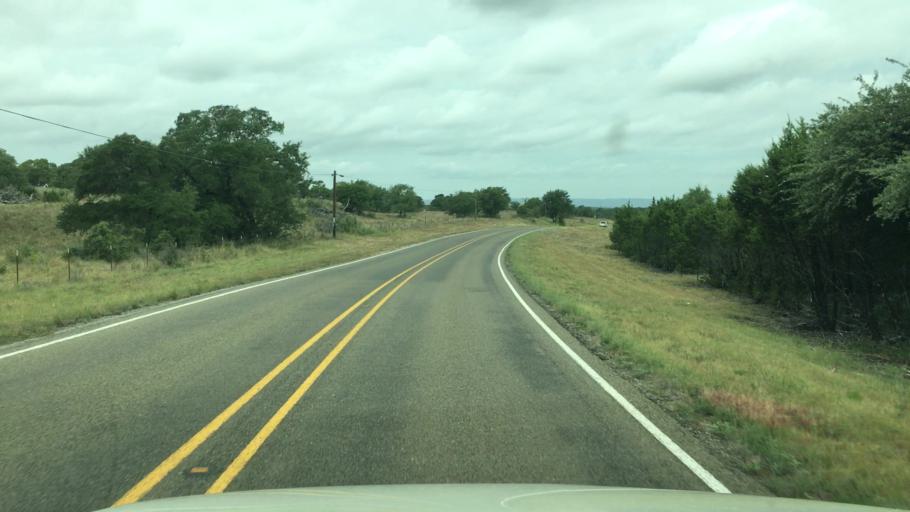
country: US
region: Texas
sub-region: Llano County
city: Horseshoe Bay
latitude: 30.4580
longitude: -98.3987
